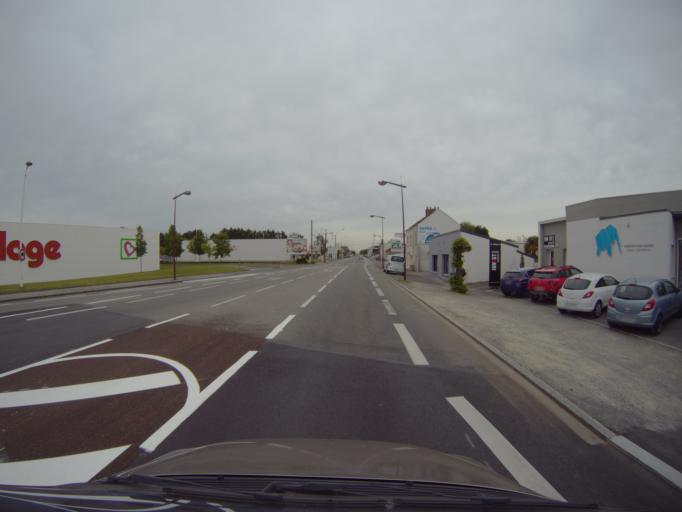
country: FR
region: Pays de la Loire
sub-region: Departement de la Loire-Atlantique
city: Les Sorinieres
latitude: 47.1618
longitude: -1.5419
